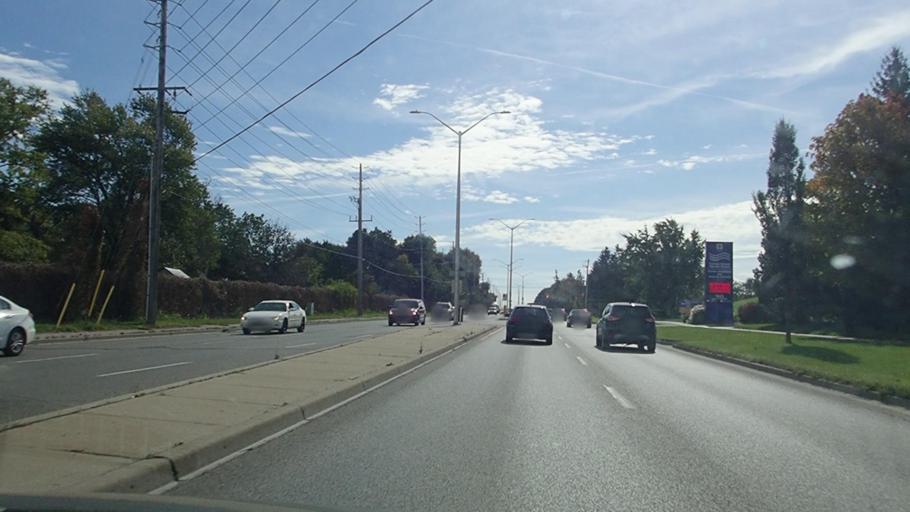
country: CA
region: Ontario
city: London
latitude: 43.0026
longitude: -81.3024
